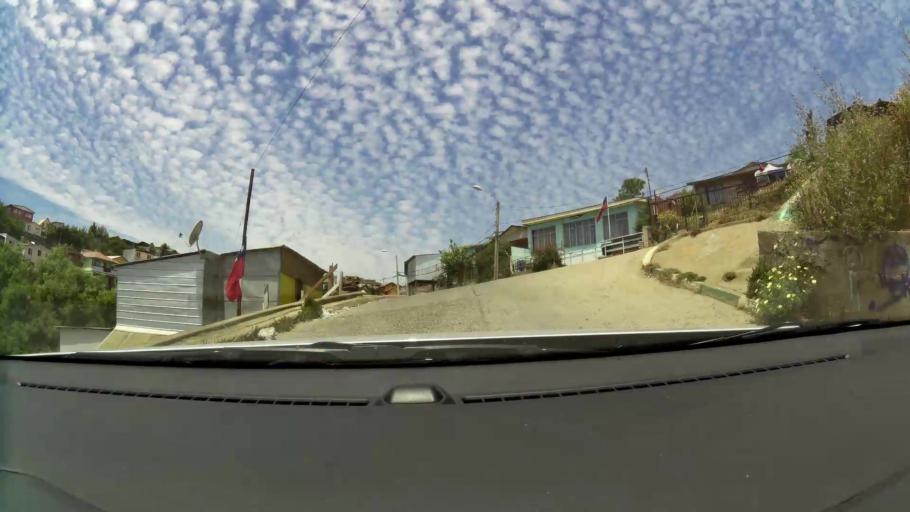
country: CL
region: Valparaiso
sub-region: Provincia de Valparaiso
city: Vina del Mar
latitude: -33.0523
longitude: -71.5670
